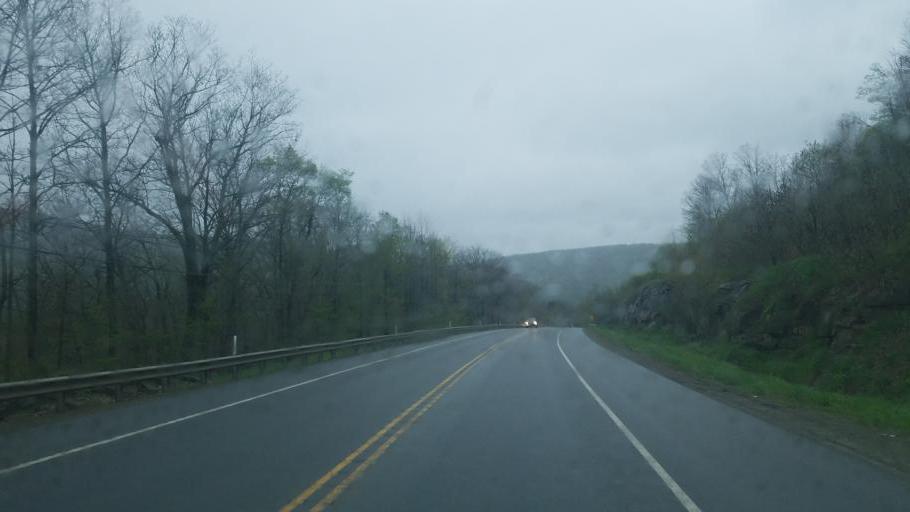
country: US
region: Pennsylvania
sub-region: McKean County
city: Port Allegany
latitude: 41.7908
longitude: -78.2312
